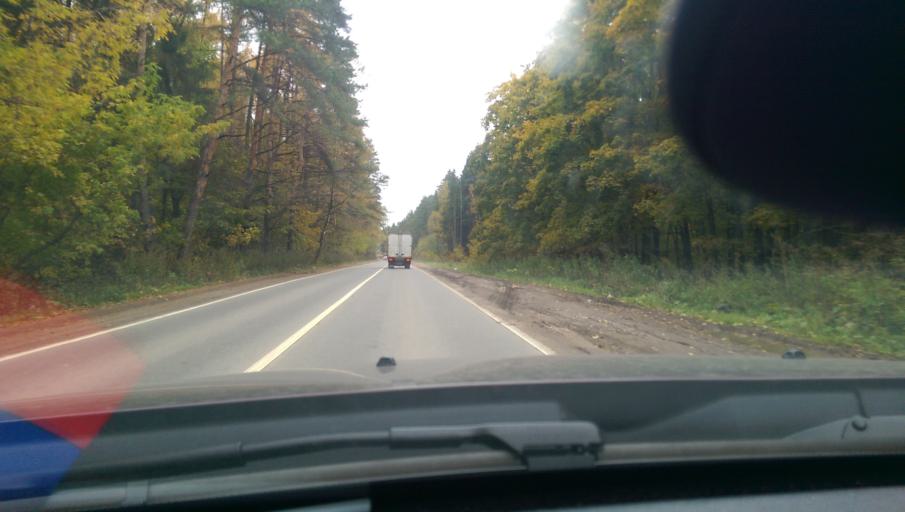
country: RU
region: Moskovskaya
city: Pirogovskiy
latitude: 55.9921
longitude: 37.7272
